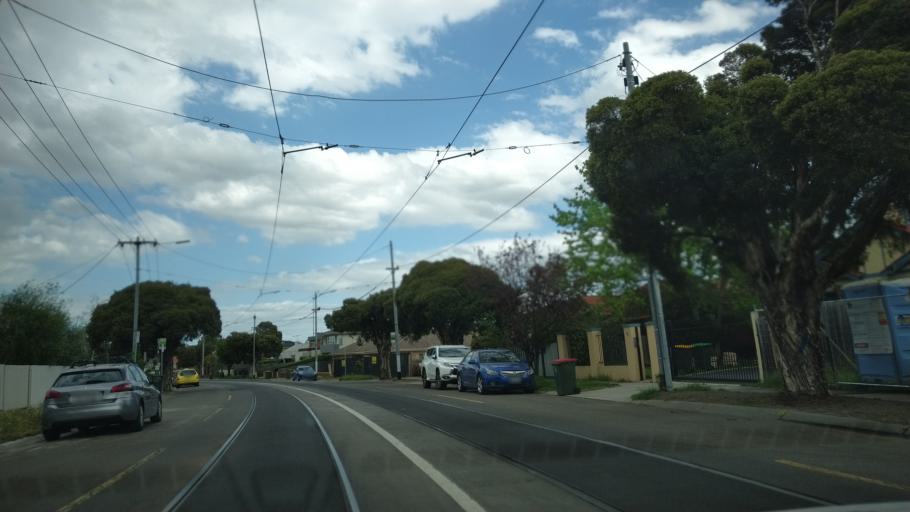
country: AU
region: Victoria
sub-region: Glen Eira
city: Carnegie
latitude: -37.8923
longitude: 145.0543
